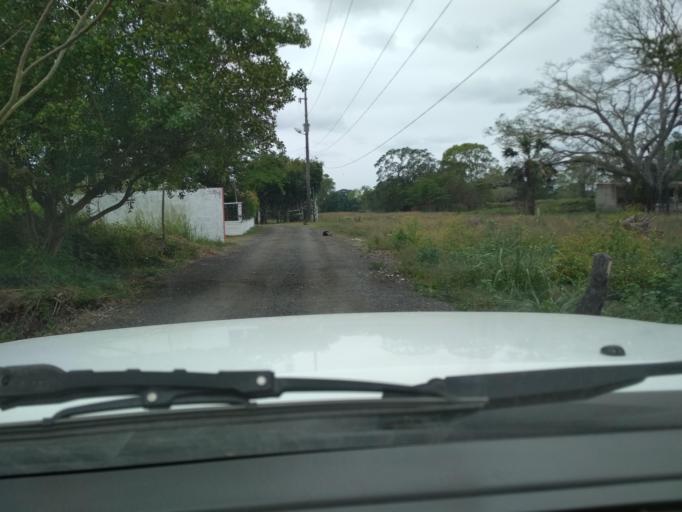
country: MX
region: Veracruz
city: Paso del Toro
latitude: 19.0479
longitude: -96.1371
